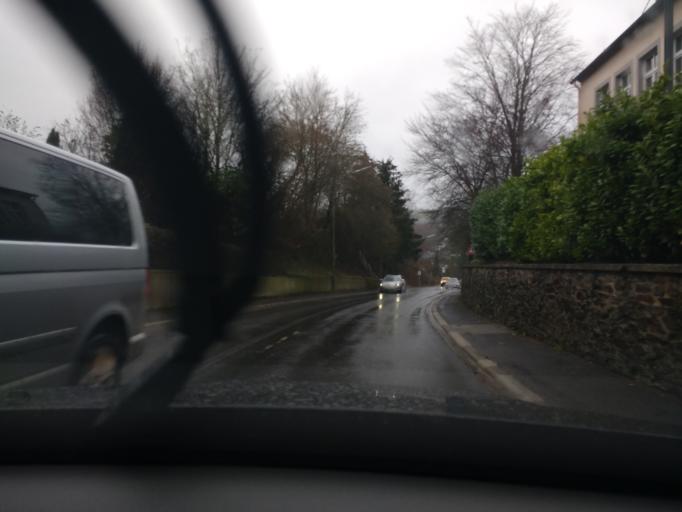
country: DE
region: Rheinland-Pfalz
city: Pluwig
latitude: 49.6898
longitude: 6.7124
